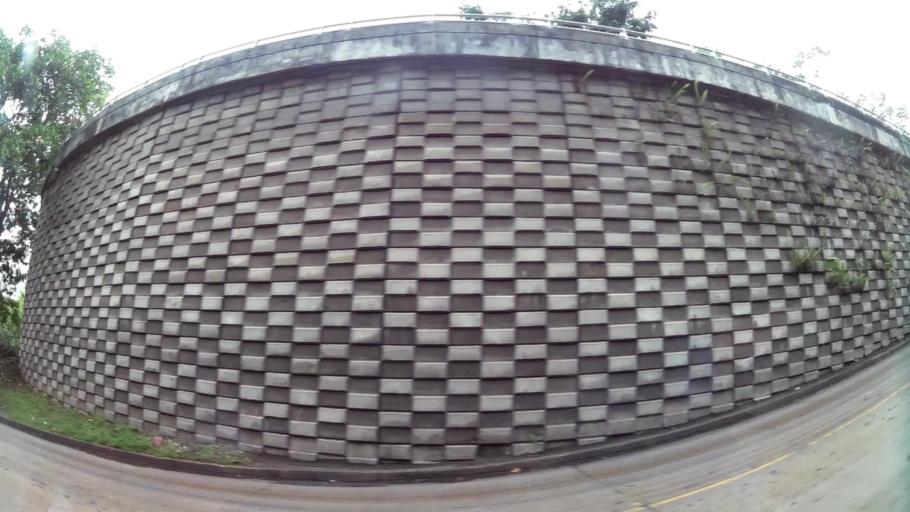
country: PA
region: Panama
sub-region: Distrito de Panama
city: Ancon
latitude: 8.9519
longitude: -79.5497
